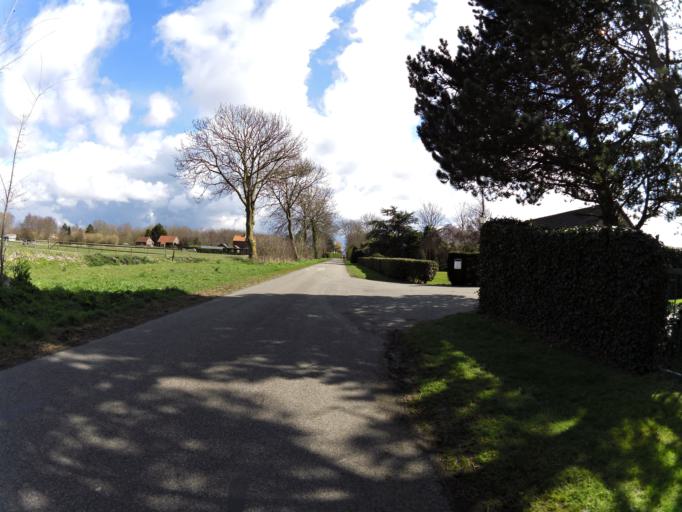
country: NL
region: South Holland
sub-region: Gemeente Hellevoetsluis
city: Nieuw-Helvoet
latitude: 51.8891
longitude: 4.0659
